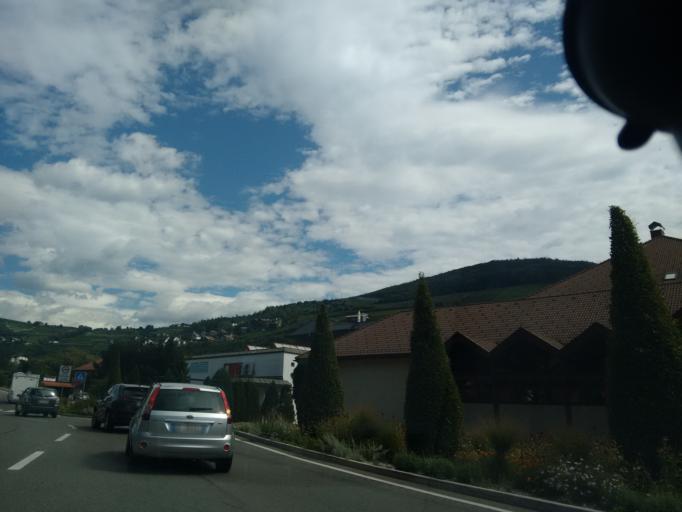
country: IT
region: Trentino-Alto Adige
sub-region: Bolzano
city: Leone-Santa Elisabetta
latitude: 46.7323
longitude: 11.6503
